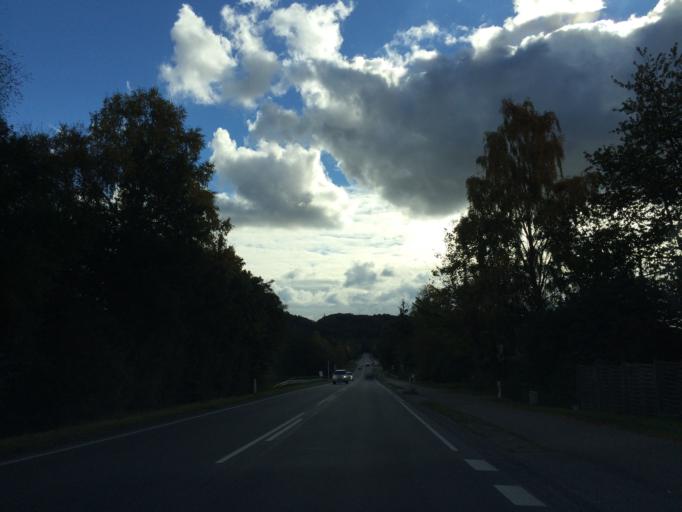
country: DK
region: Central Jutland
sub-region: Skanderborg Kommune
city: Ry
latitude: 56.1068
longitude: 9.7846
